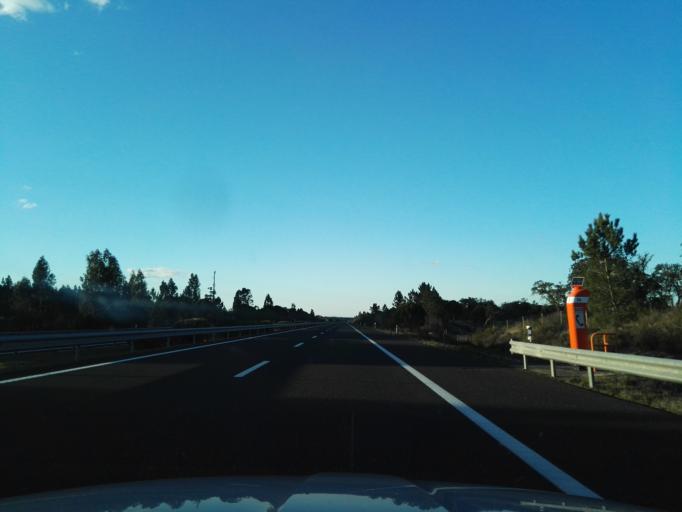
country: PT
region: Santarem
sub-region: Benavente
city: Poceirao
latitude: 38.8044
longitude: -8.7005
